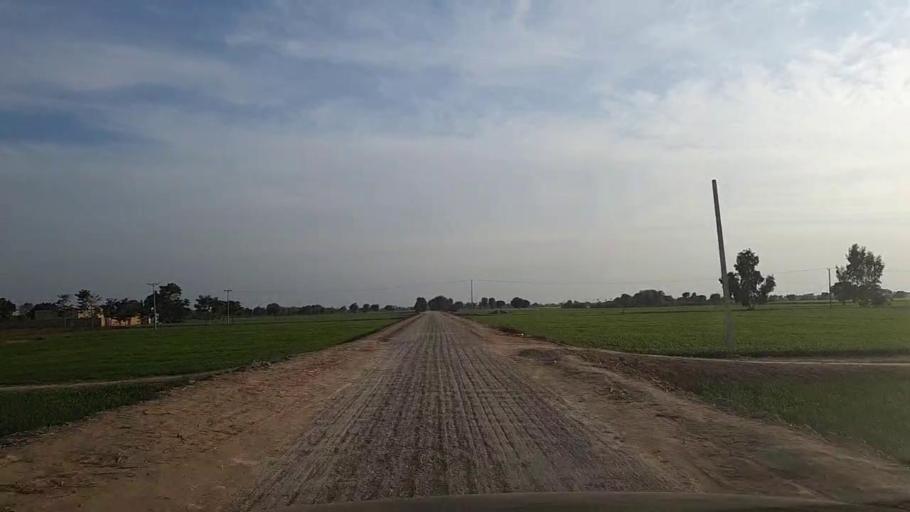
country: PK
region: Sindh
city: Jam Sahib
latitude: 26.4440
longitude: 68.5717
